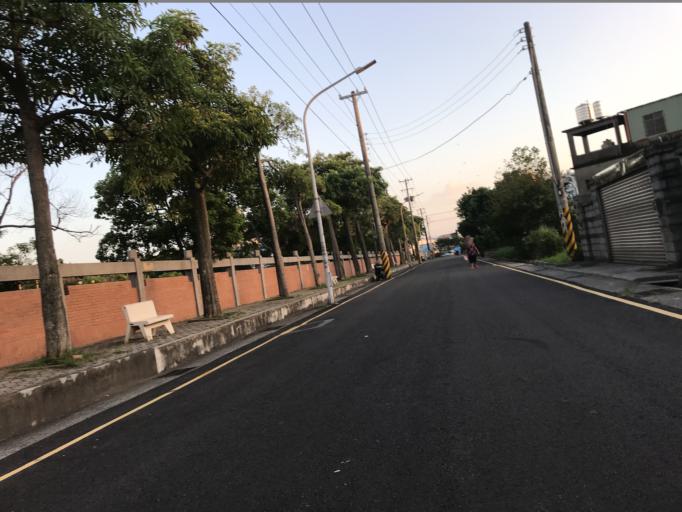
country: TW
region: Taiwan
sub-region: Hsinchu
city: Hsinchu
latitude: 24.8064
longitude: 120.9403
